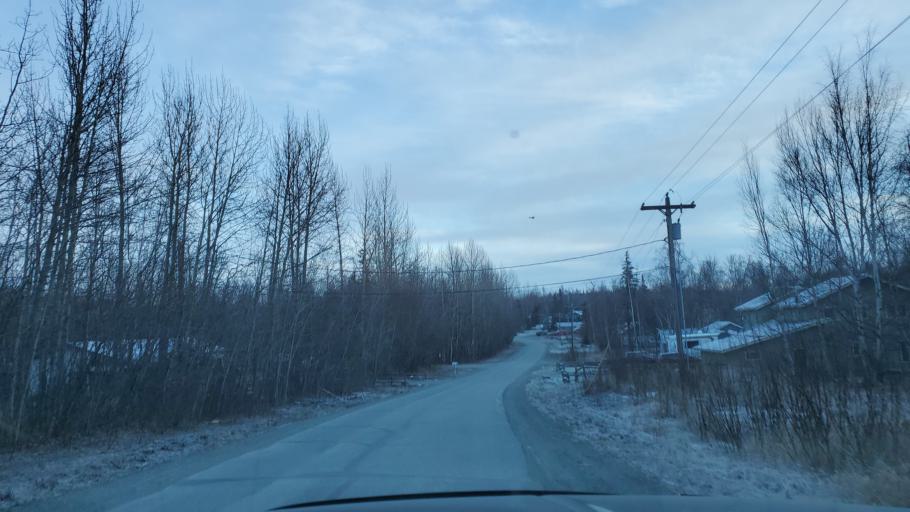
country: US
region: Alaska
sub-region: Matanuska-Susitna Borough
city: Lakes
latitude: 61.6075
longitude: -149.3150
